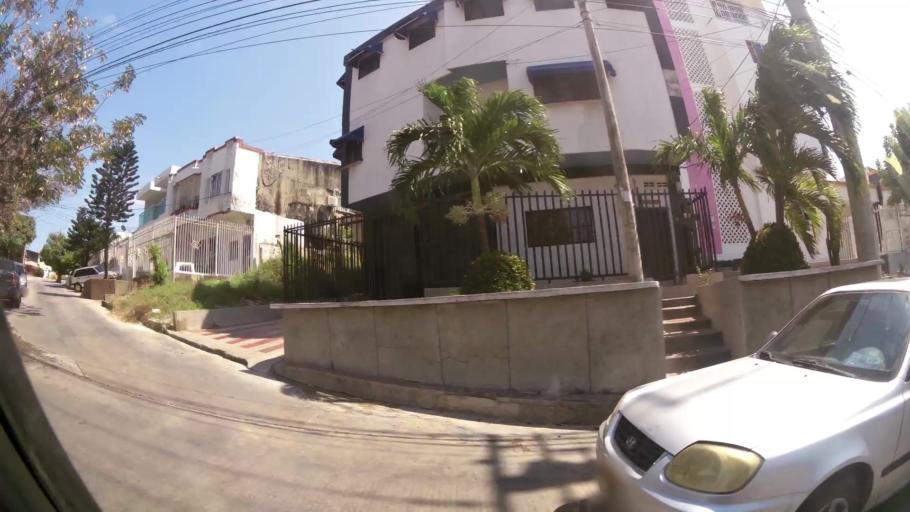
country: CO
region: Atlantico
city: Barranquilla
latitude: 10.9860
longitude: -74.8326
